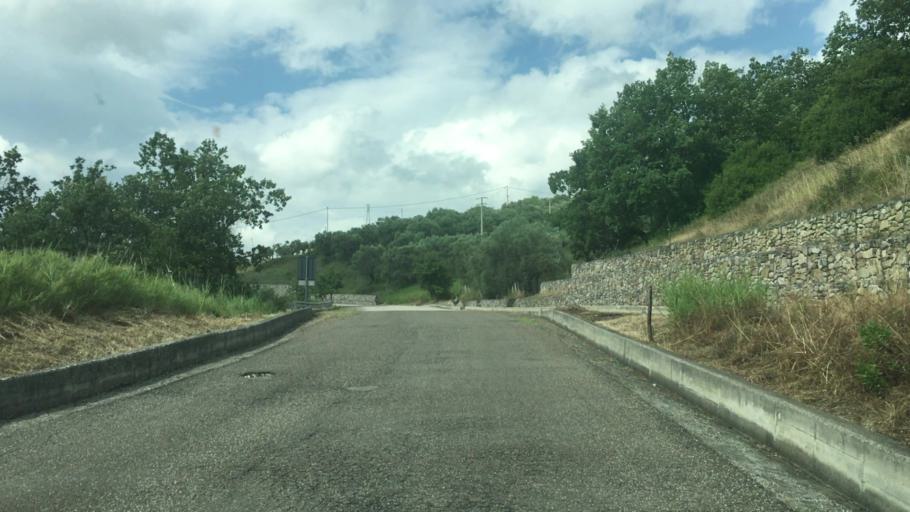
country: IT
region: Basilicate
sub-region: Provincia di Matera
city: San Mauro Forte
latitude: 40.4825
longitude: 16.2681
